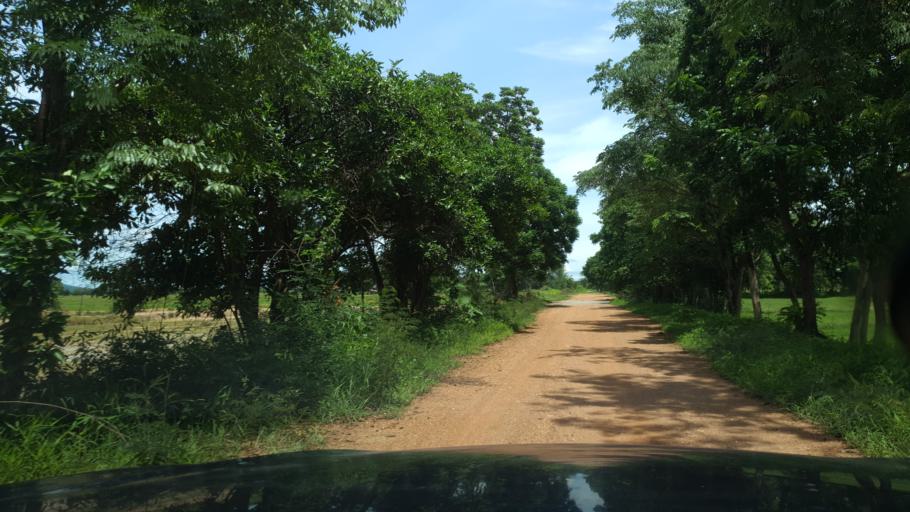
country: TH
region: Sukhothai
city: Ban Na
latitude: 17.0702
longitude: 99.6989
